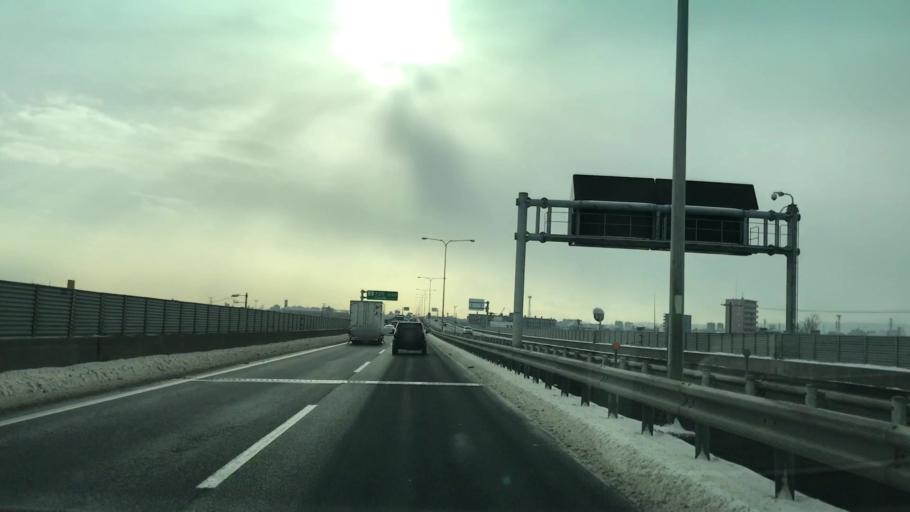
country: JP
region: Hokkaido
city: Sapporo
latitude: 43.0556
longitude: 141.4279
